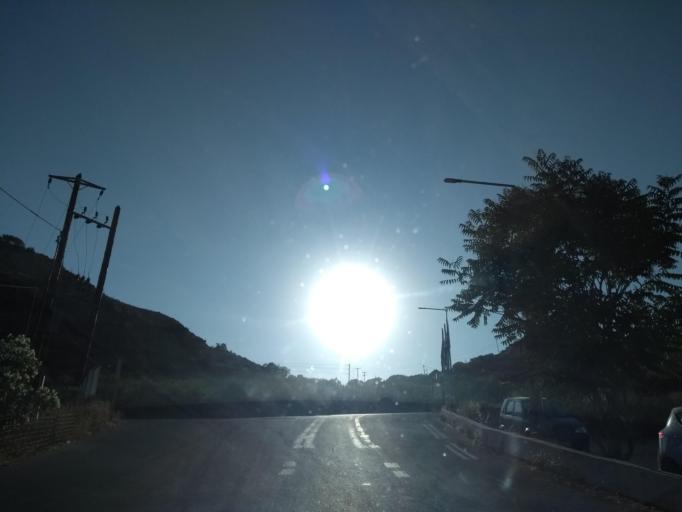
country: GR
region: Crete
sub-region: Nomos Chanias
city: Kalivai
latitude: 35.4674
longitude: 24.1532
